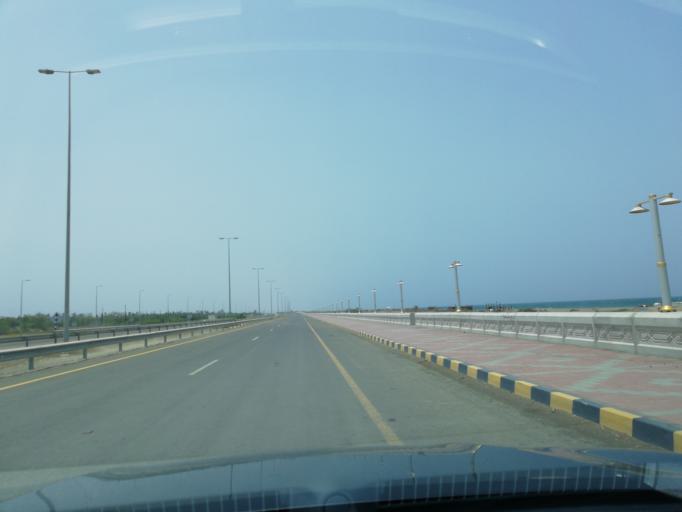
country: OM
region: Al Batinah
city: Al Liwa'
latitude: 24.6220
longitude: 56.5328
